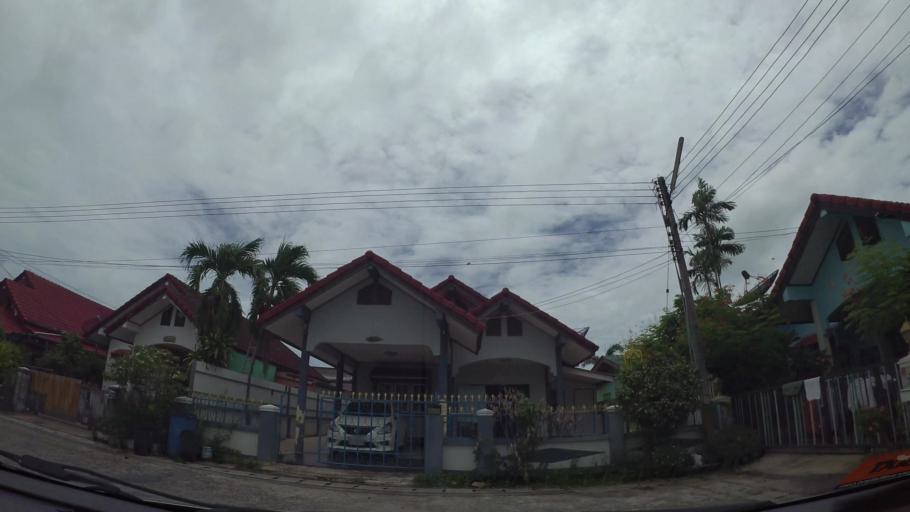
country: TH
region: Chon Buri
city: Sattahip
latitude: 12.7593
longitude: 100.8947
